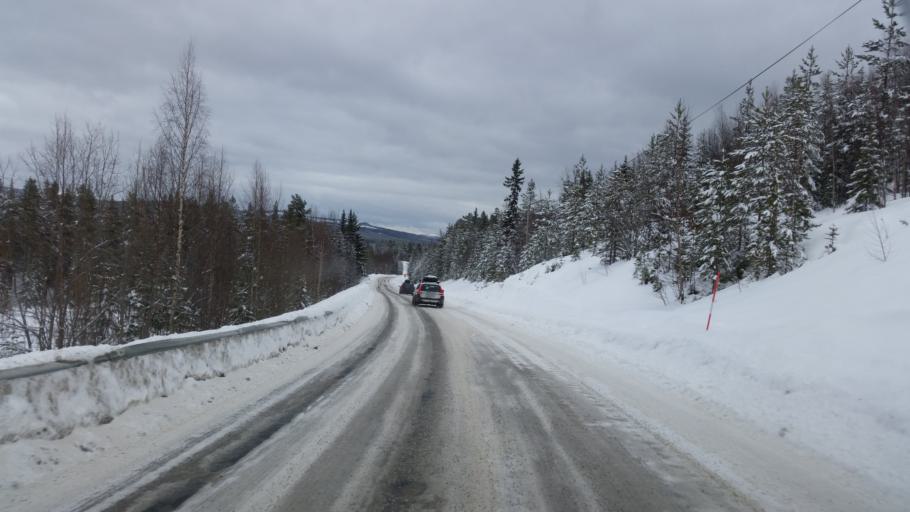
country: SE
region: Jaemtland
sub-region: Bergs Kommun
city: Hoverberg
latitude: 62.4640
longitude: 14.5240
